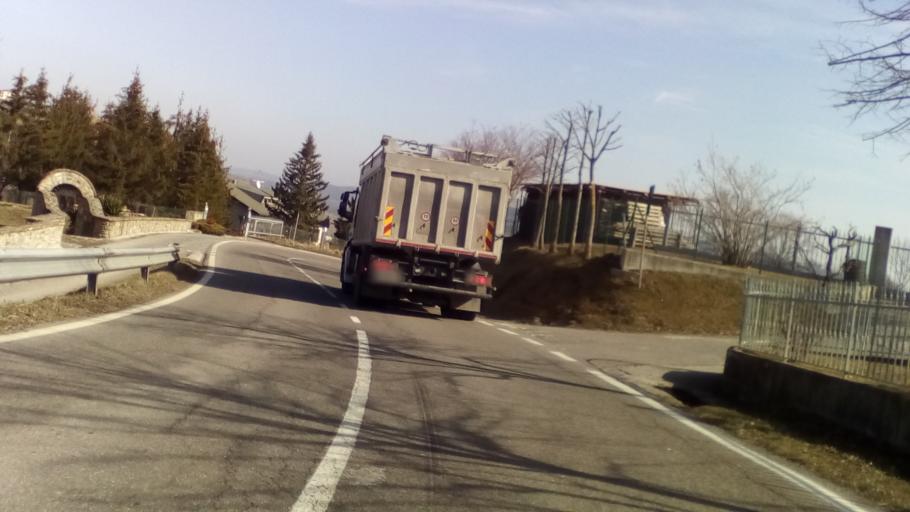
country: IT
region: Emilia-Romagna
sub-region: Provincia di Modena
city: Lama
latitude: 44.3122
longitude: 10.7625
